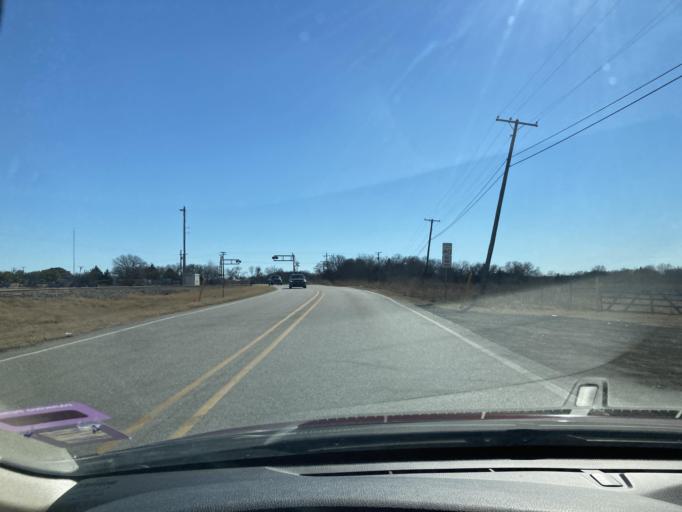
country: US
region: Texas
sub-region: Navarro County
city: Corsicana
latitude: 32.0692
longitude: -96.4637
